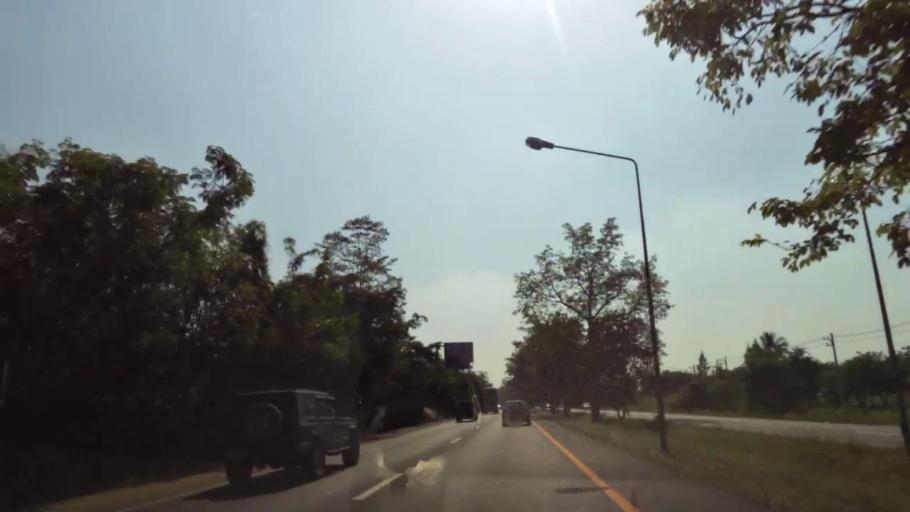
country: TH
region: Phichit
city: Bueng Na Rang
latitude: 16.0331
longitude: 100.1159
